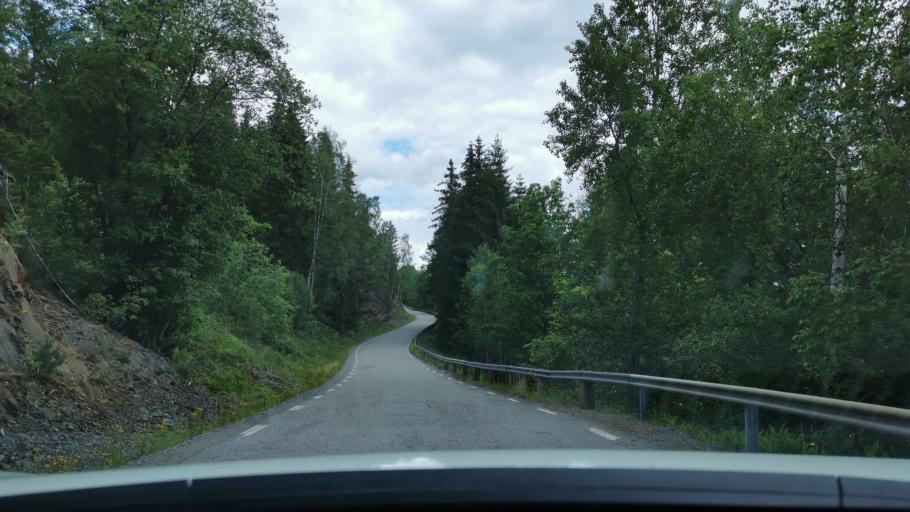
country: SE
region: Vaestra Goetaland
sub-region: Bengtsfors Kommun
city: Dals Langed
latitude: 58.8297
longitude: 12.3310
